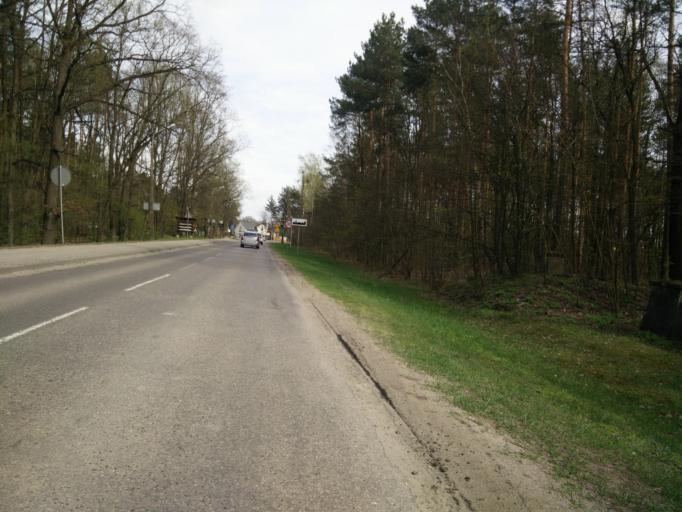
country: PL
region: Masovian Voivodeship
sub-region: Powiat warszawski zachodni
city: Izabelin
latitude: 52.2910
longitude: 20.8364
